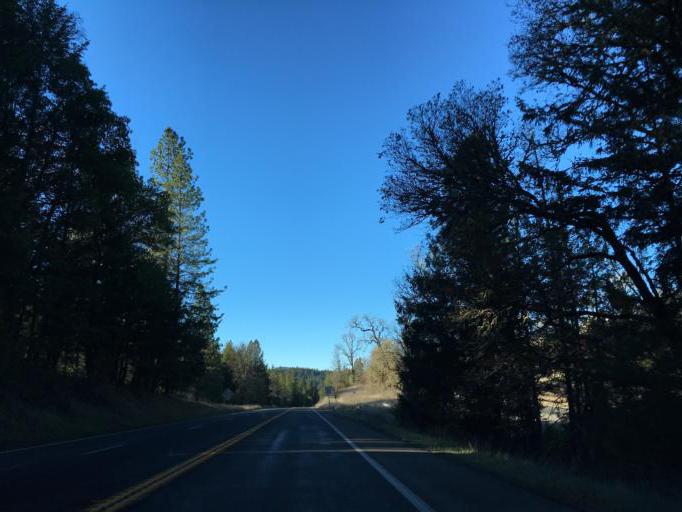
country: US
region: California
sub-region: Mendocino County
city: Laytonville
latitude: 39.7119
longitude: -123.4934
